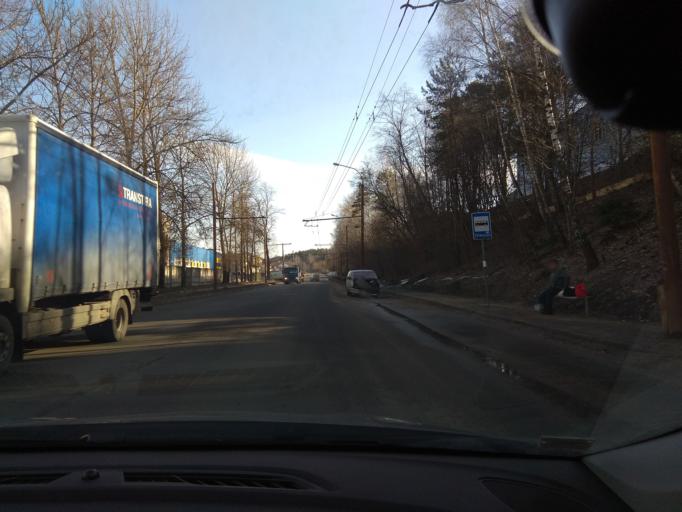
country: LT
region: Vilnius County
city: Lazdynai
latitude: 54.6498
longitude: 25.1861
